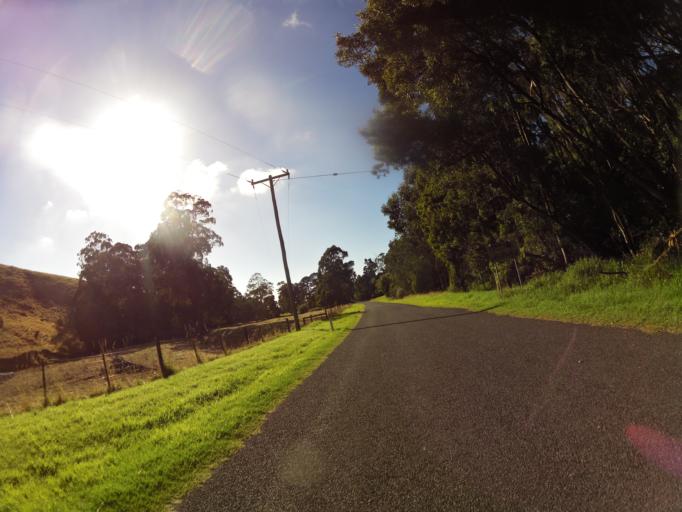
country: AU
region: Victoria
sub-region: Colac-Otway
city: Apollo Bay
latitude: -38.7639
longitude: 143.6316
